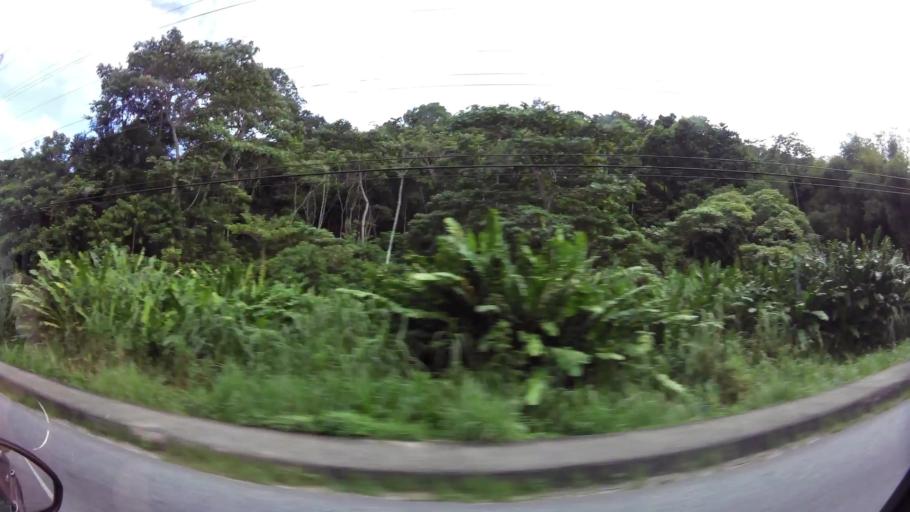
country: TT
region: Diego Martin
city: Petit Valley
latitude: 10.7142
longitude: -61.4664
